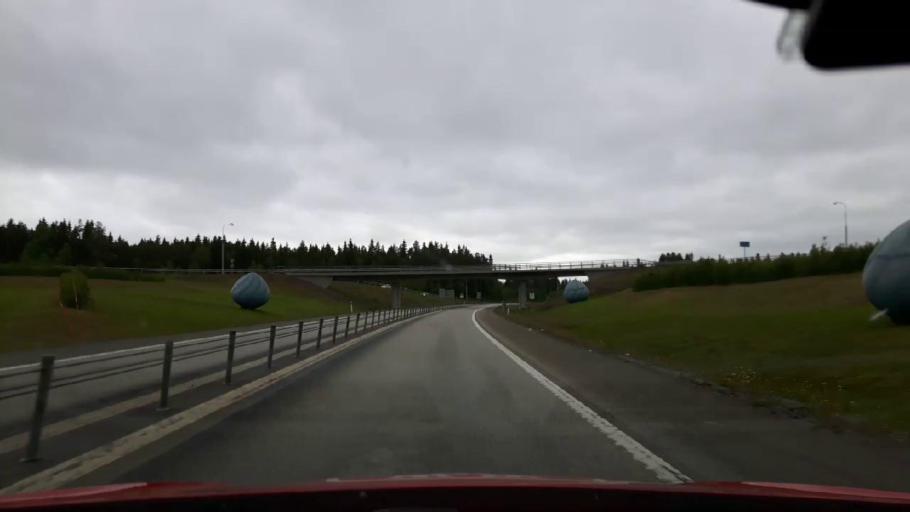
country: SE
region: Jaemtland
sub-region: OEstersunds Kommun
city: Ostersund
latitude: 63.1818
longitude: 14.6893
